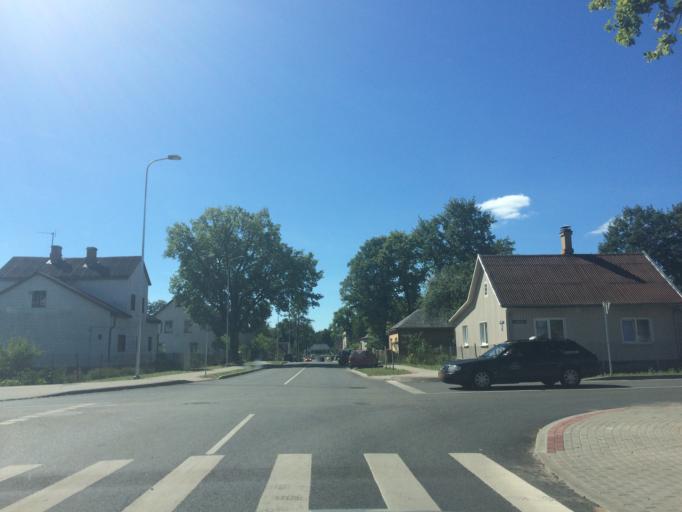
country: LV
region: Rezekne
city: Rezekne
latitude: 56.5089
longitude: 27.3414
